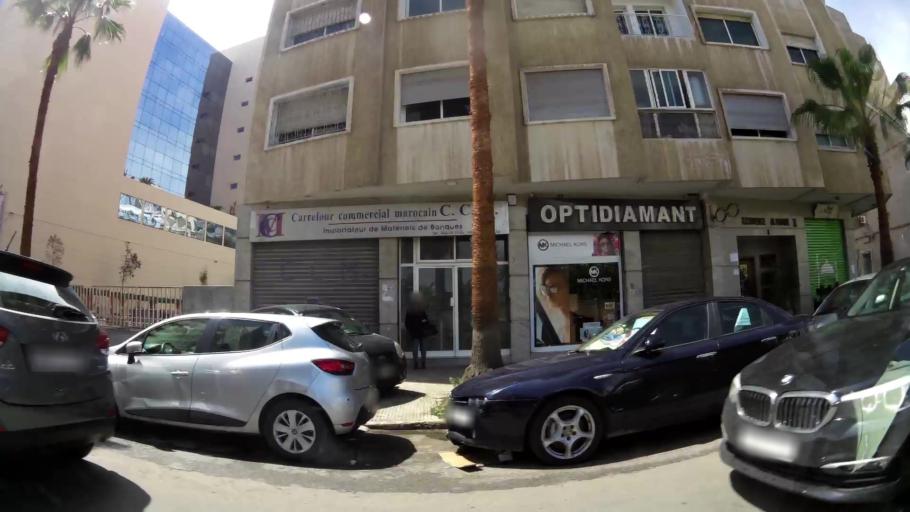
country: MA
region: Grand Casablanca
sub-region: Casablanca
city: Casablanca
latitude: 33.5813
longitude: -7.6230
